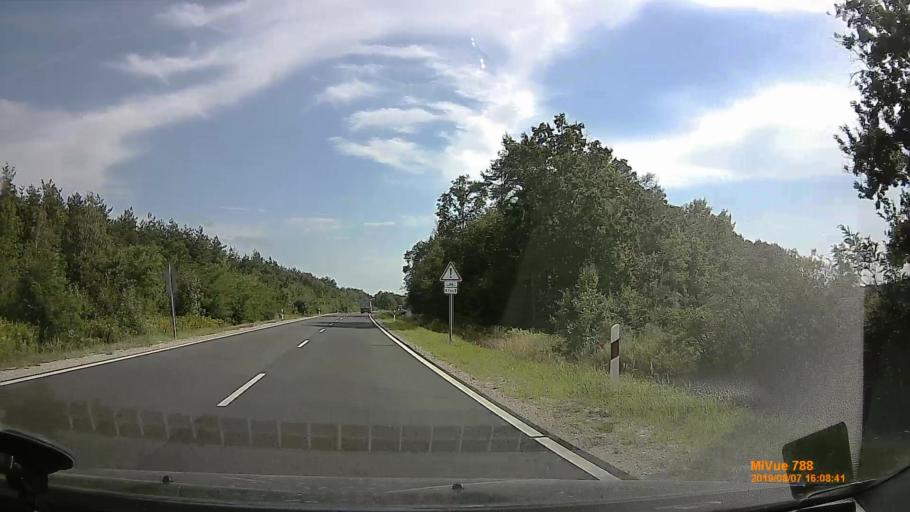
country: HU
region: Zala
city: Zalalovo
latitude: 46.9046
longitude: 16.6038
